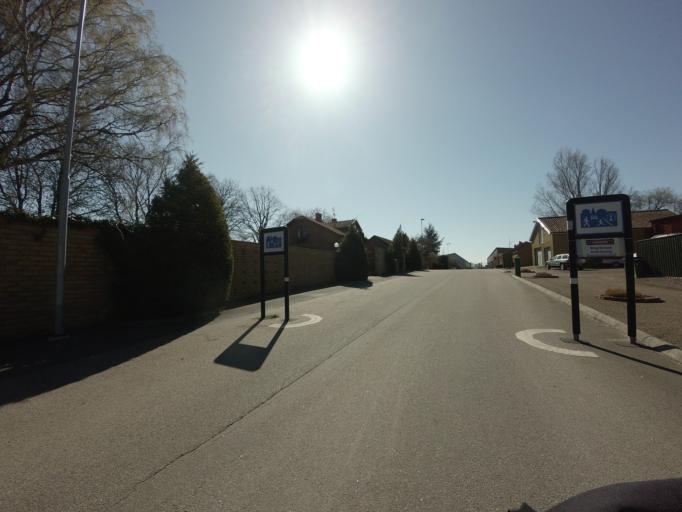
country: SE
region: Skane
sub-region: Malmo
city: Oxie
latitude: 55.4643
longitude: 13.1352
